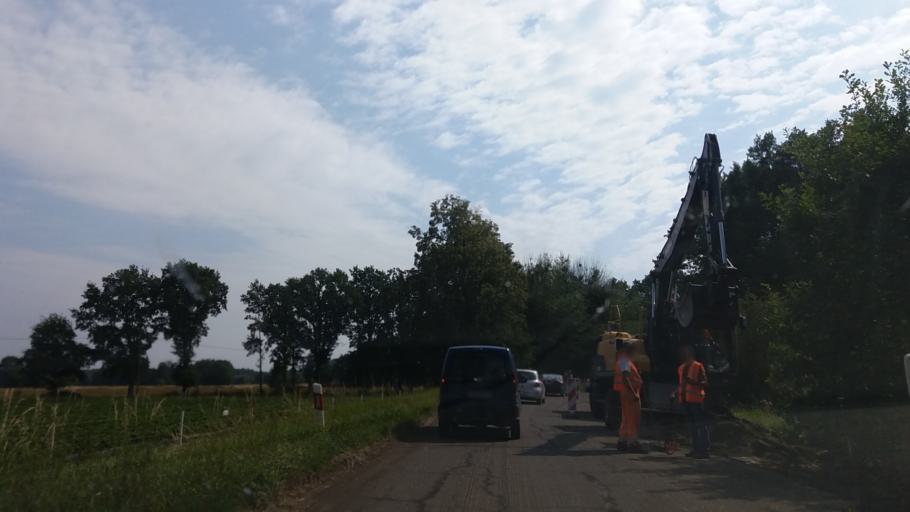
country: PL
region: Lubusz
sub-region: Powiat strzelecko-drezdenecki
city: Stare Kurowo
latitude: 52.7683
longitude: 15.6456
